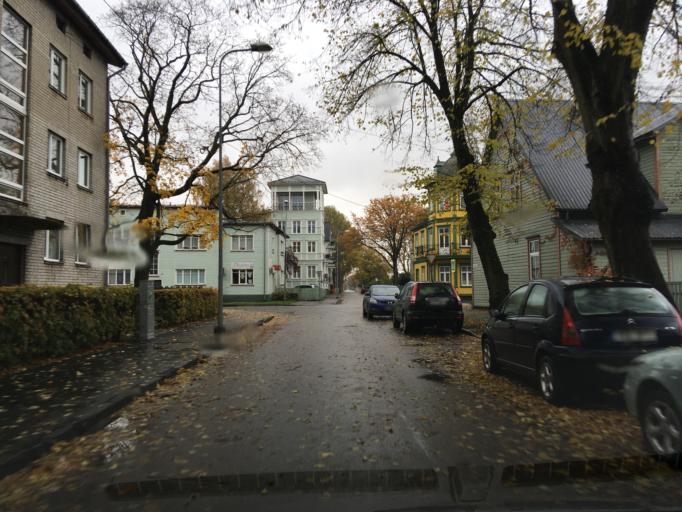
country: EE
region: Paernumaa
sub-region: Paernu linn
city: Parnu
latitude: 58.3810
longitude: 24.5049
